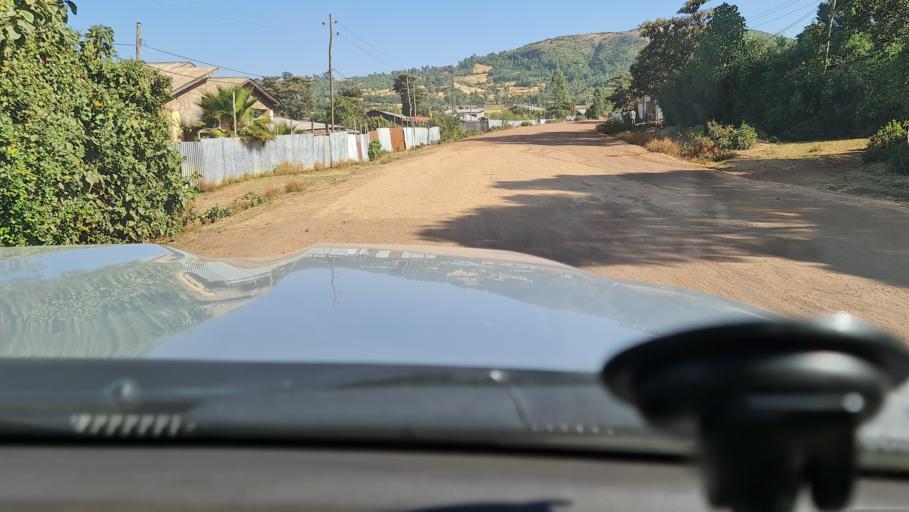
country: ET
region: Oromiya
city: Waliso
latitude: 8.6097
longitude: 37.9224
